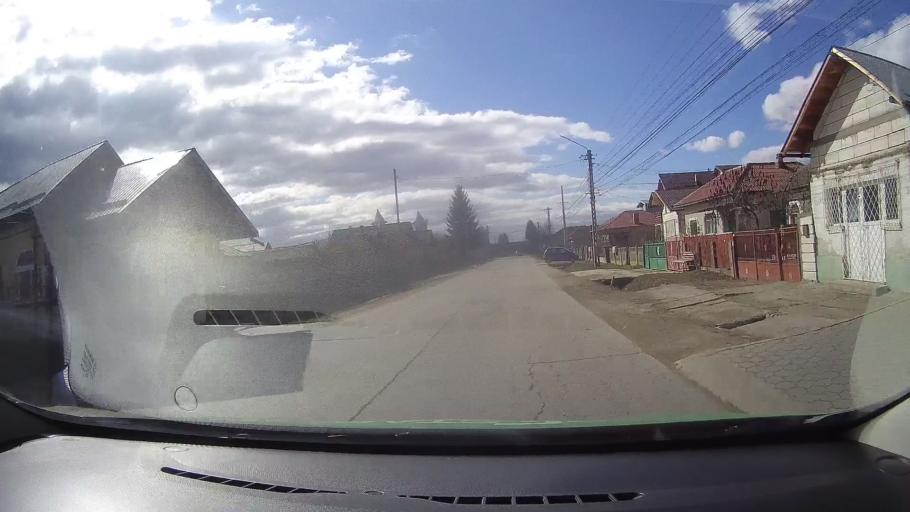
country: RO
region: Dambovita
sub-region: Comuna Branesti
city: Branesti
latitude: 45.0344
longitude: 25.4142
